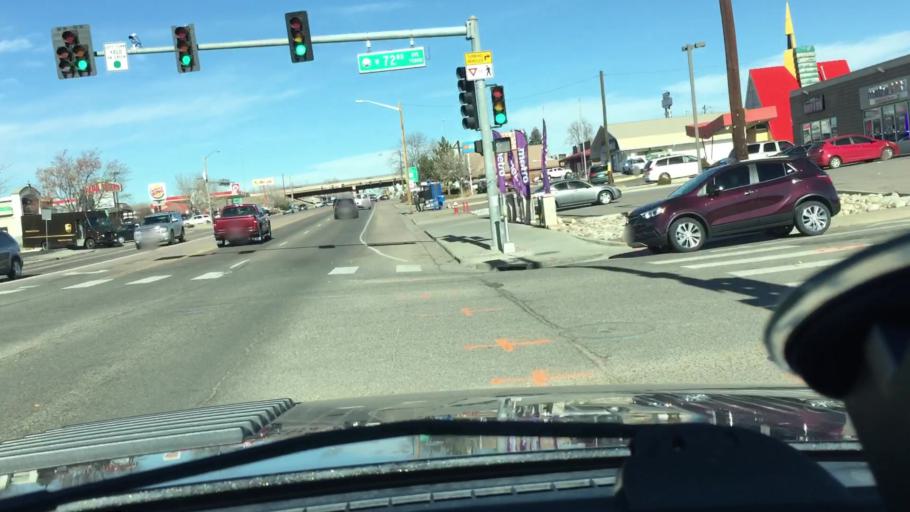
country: US
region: Colorado
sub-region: Adams County
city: Twin Lakes
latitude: 39.8272
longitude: -105.0061
